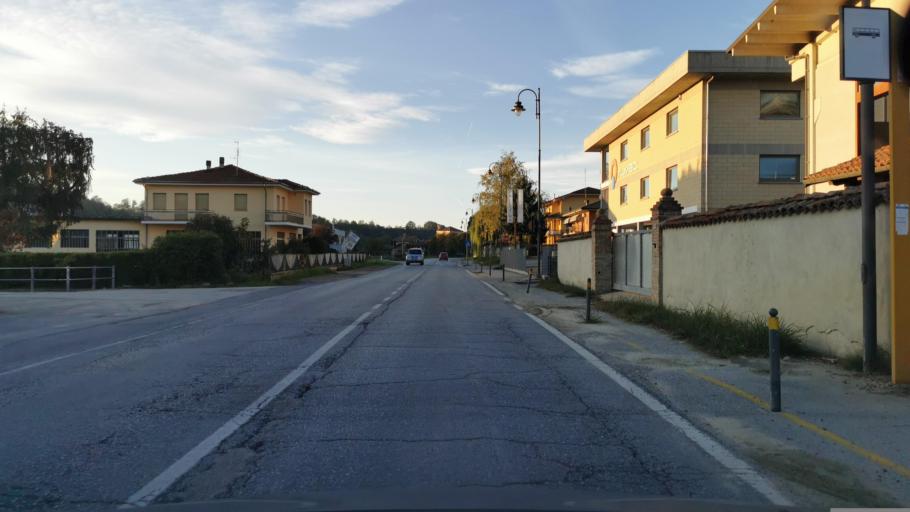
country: IT
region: Piedmont
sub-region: Provincia di Cuneo
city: Dogliani
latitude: 44.5405
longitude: 7.9302
